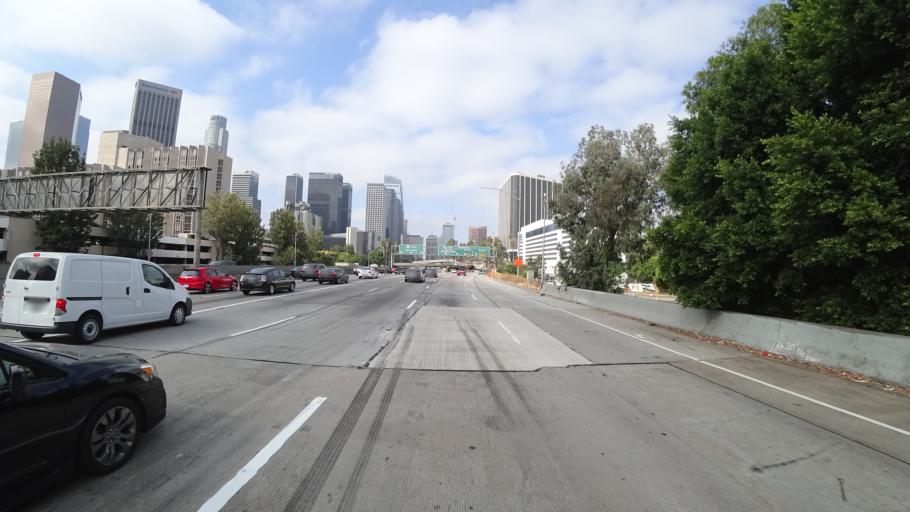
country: US
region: California
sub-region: Los Angeles County
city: Los Angeles
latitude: 34.0588
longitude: -118.2535
